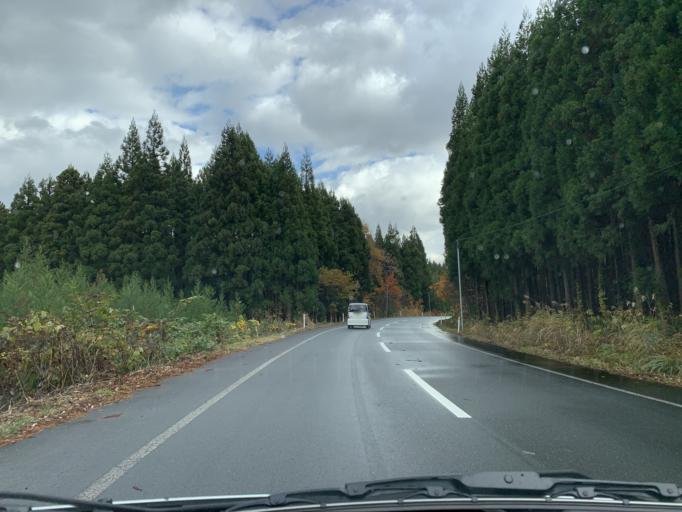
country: JP
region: Iwate
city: Mizusawa
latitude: 39.1140
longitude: 140.9547
